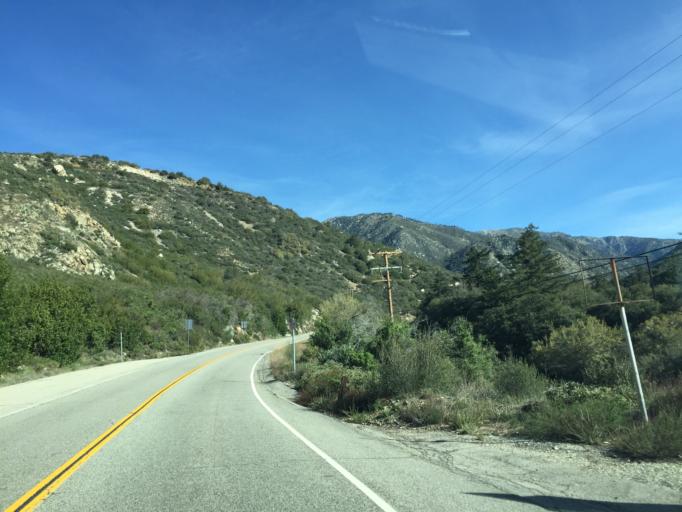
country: US
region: California
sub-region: San Bernardino County
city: San Antonio Heights
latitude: 34.2233
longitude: -117.6680
